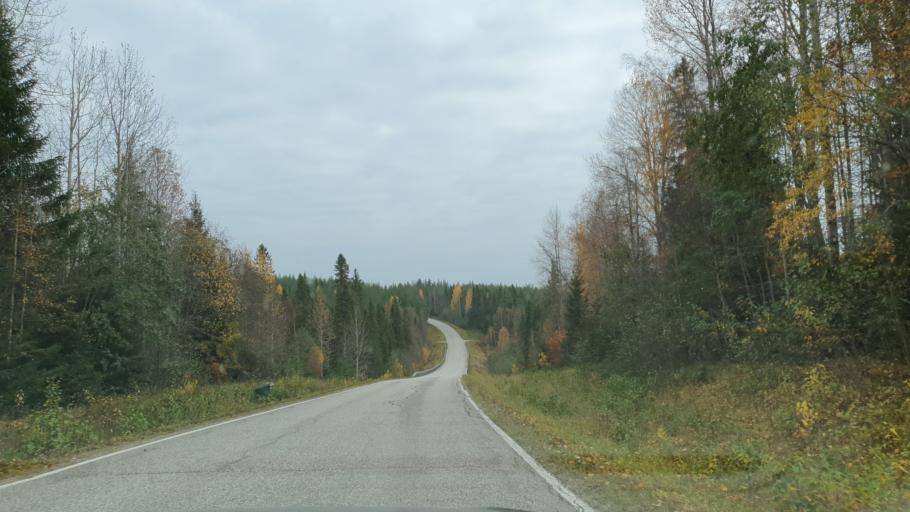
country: FI
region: Kainuu
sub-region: Kajaani
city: Ristijaervi
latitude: 64.4741
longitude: 28.2873
